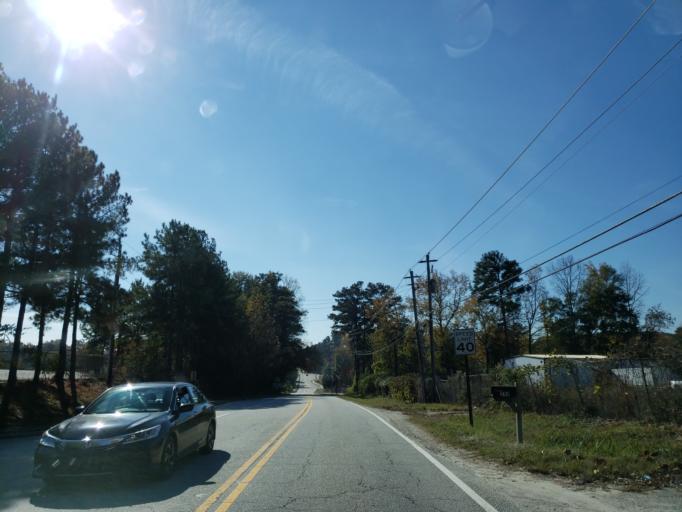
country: US
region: Georgia
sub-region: Cobb County
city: Mableton
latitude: 33.7784
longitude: -84.5465
